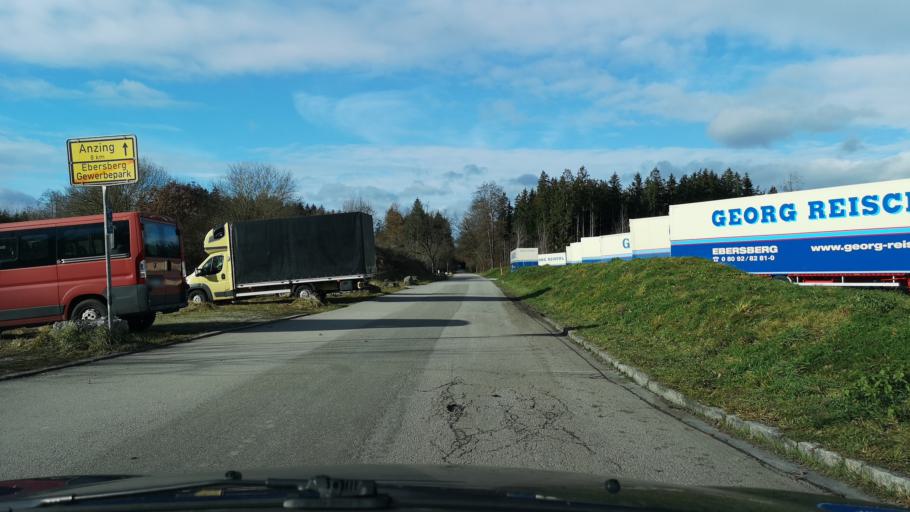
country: DE
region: Bavaria
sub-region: Upper Bavaria
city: Ebersberg
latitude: 48.0960
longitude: 11.9549
